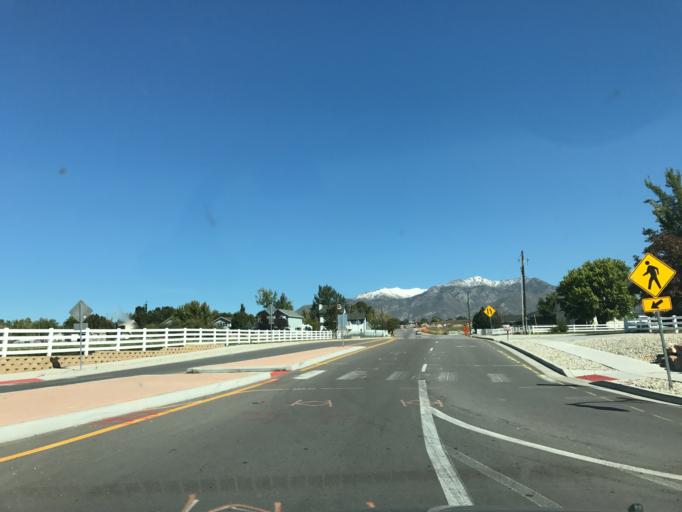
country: US
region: Utah
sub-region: Davis County
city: Layton
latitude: 41.0890
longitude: -111.9447
